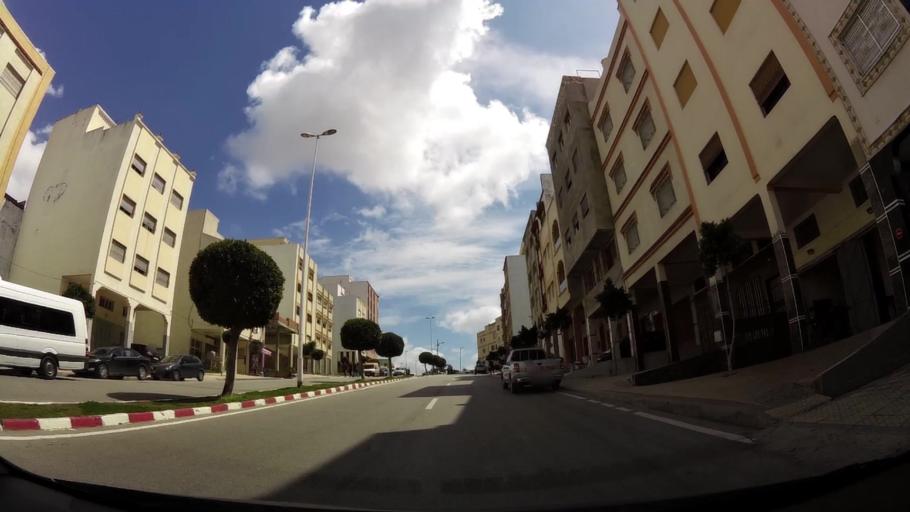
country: MA
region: Tanger-Tetouan
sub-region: Tanger-Assilah
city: Tangier
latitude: 35.7509
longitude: -5.8307
